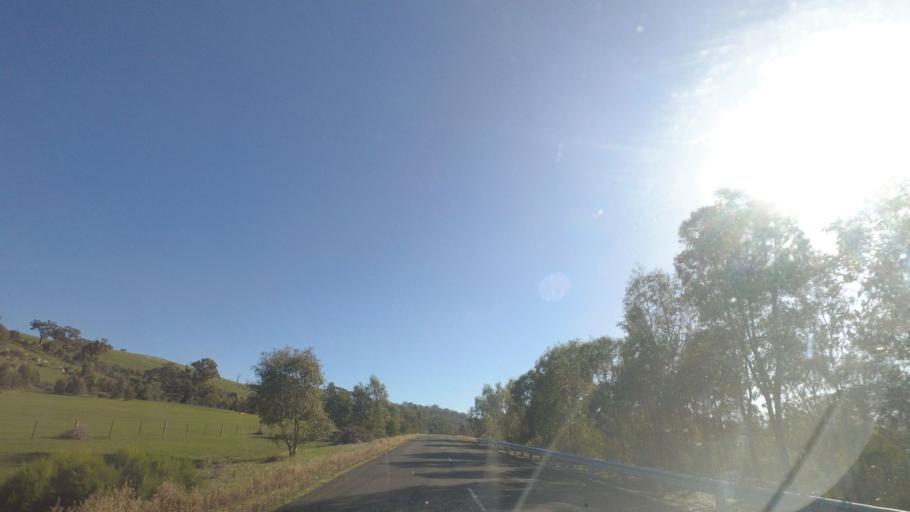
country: AU
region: Victoria
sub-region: Mount Alexander
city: Castlemaine
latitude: -37.0462
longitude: 144.2837
